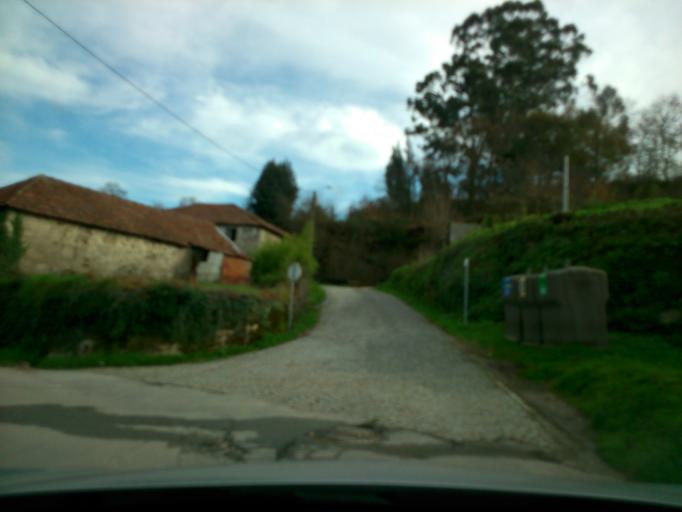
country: PT
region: Porto
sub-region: Amarante
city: Figueiro
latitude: 41.2926
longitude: -8.2040
